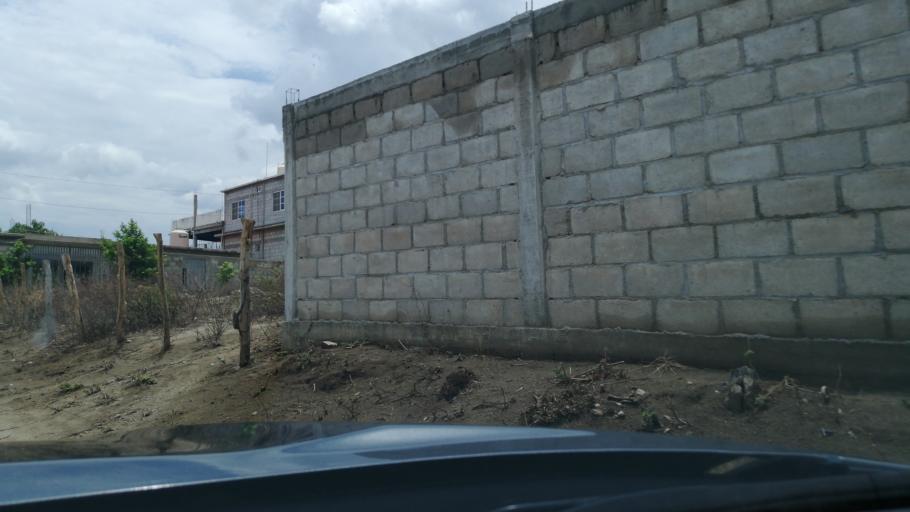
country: MX
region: Oaxaca
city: Santa Maria Jalapa del Marques
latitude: 16.4519
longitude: -95.4422
